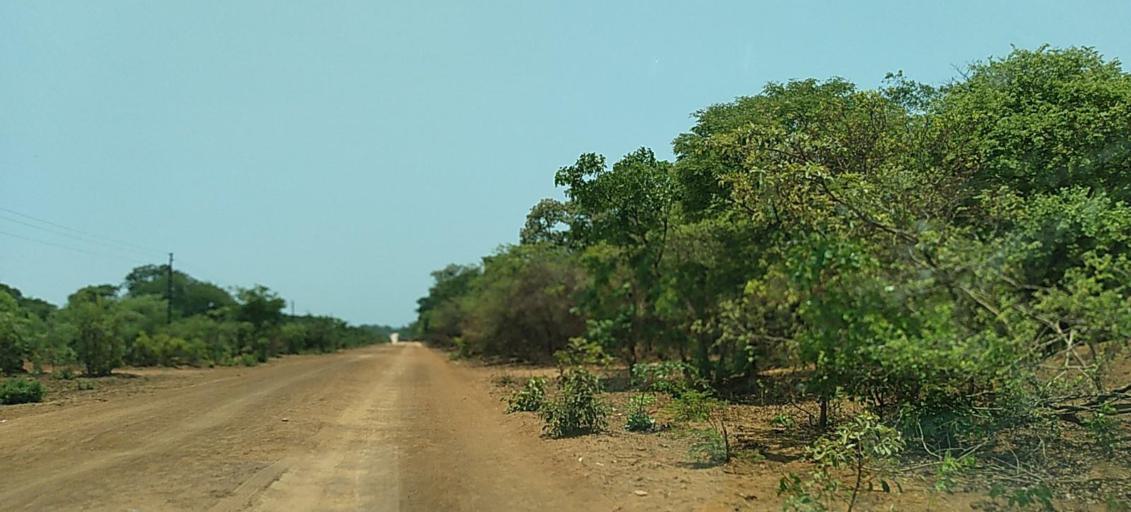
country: ZM
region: Copperbelt
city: Mpongwe
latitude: -13.8208
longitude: 27.8417
